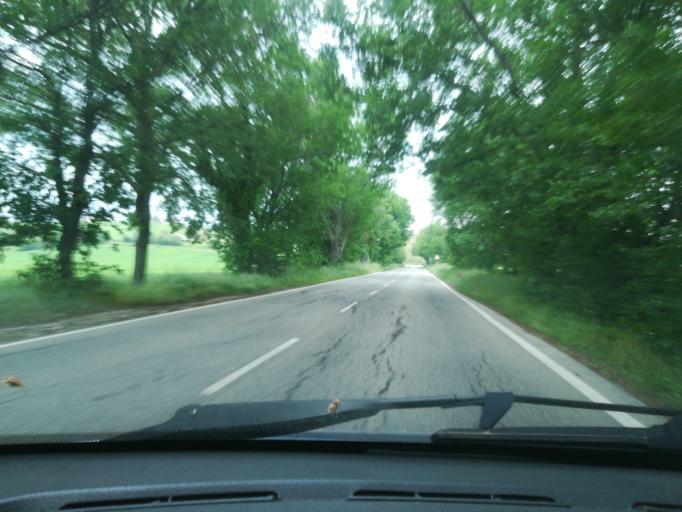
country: IT
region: The Marches
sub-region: Provincia di Macerata
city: Pollenza
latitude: 43.2897
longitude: 13.3806
